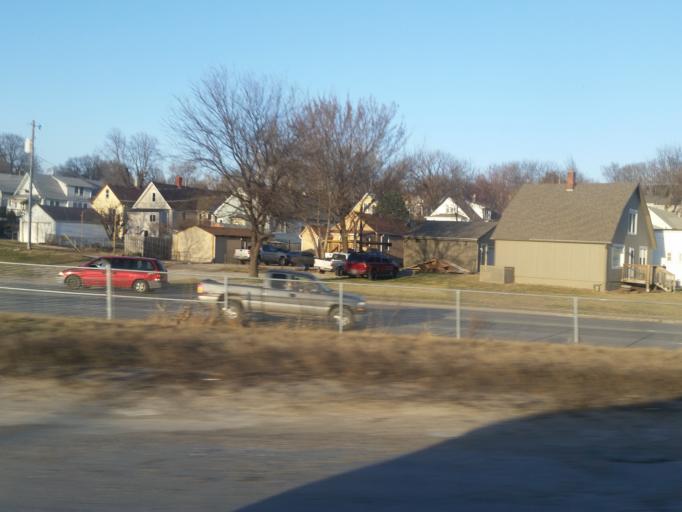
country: US
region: Nebraska
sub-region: Douglas County
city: Omaha
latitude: 41.1982
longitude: -95.9440
